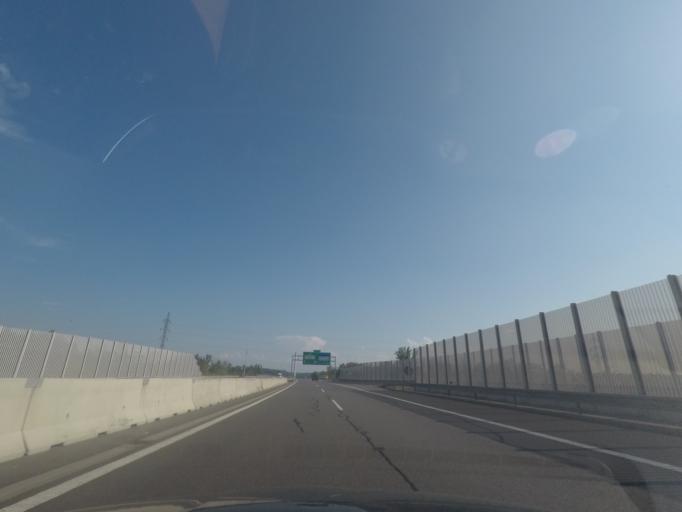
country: PL
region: Silesian Voivodeship
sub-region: Powiat raciborski
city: Chalupki
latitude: 49.8925
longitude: 18.3034
